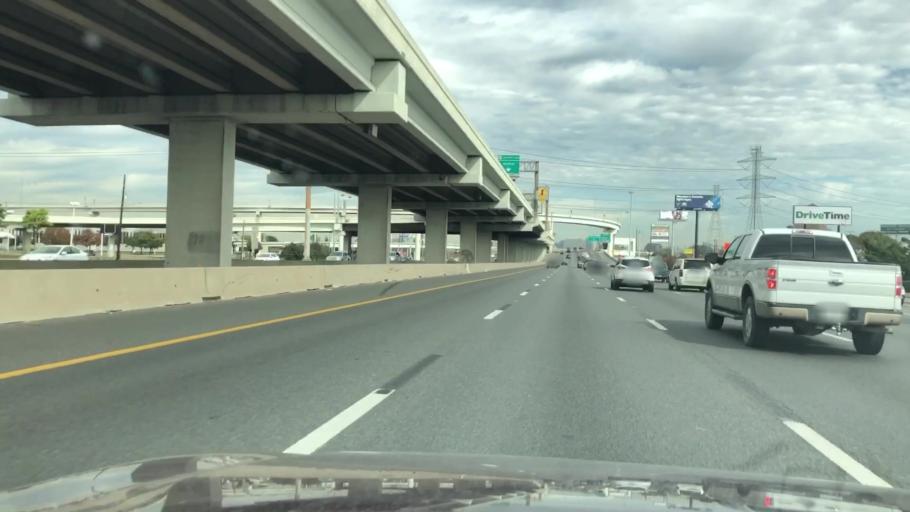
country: US
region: Texas
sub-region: Harris County
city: Bellaire
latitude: 29.7196
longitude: -95.4958
